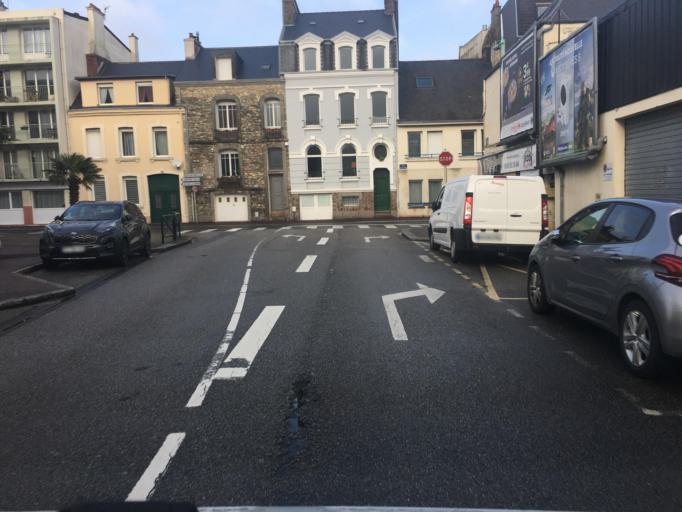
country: FR
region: Lower Normandy
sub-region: Departement de la Manche
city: Cherbourg-Octeville
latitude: 49.6388
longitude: -1.6061
